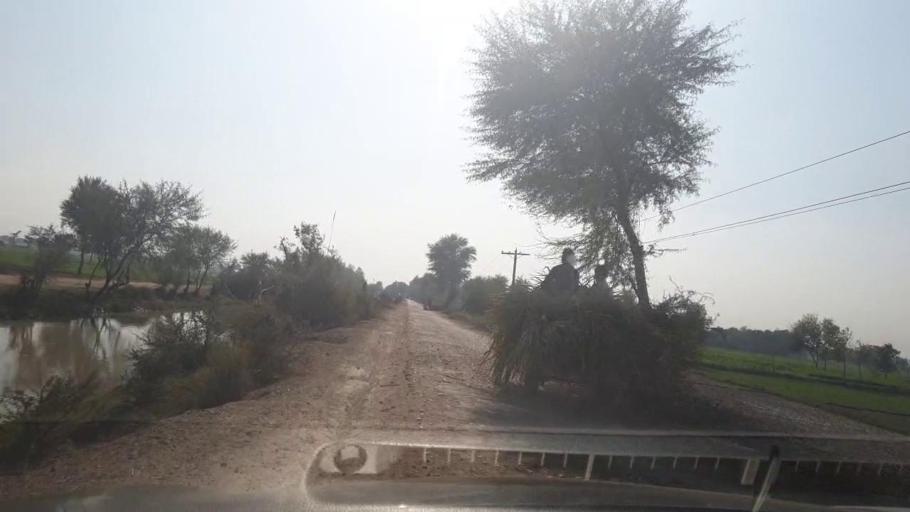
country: PK
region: Sindh
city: Ubauro
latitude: 28.1400
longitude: 69.6497
